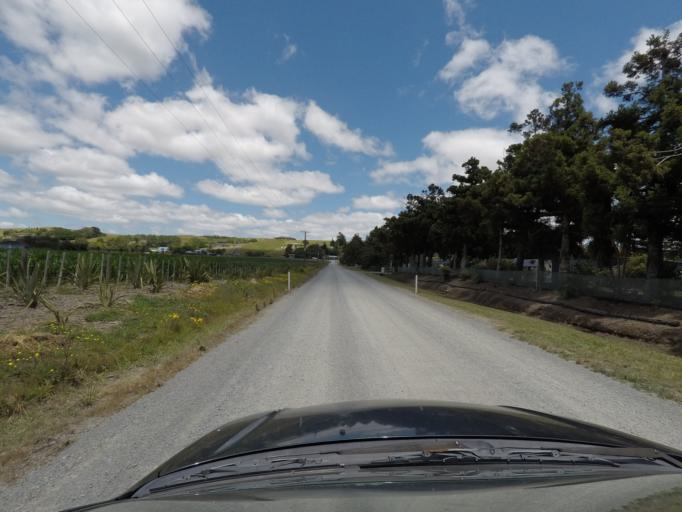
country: NZ
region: Northland
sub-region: Whangarei
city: Ruakaka
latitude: -35.9985
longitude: 174.4779
